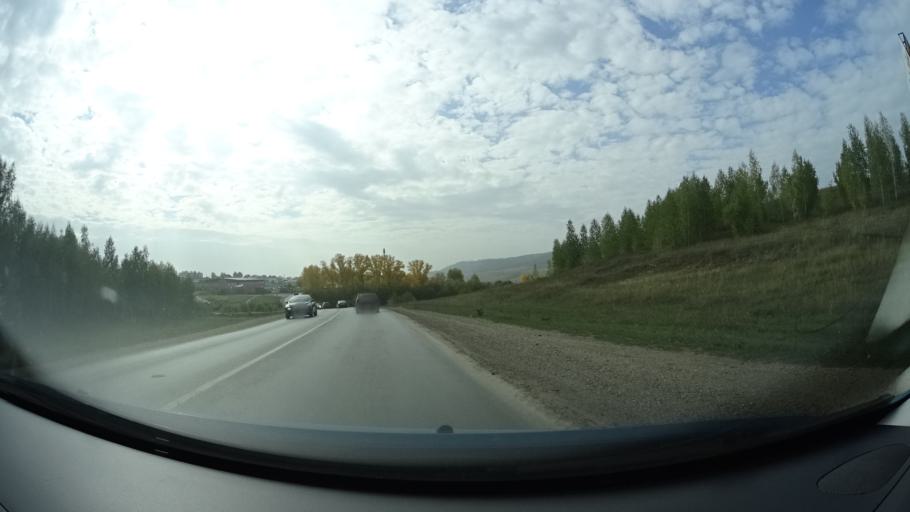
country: RU
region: Bashkortostan
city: Oktyabr'skiy
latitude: 54.5180
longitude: 53.5346
